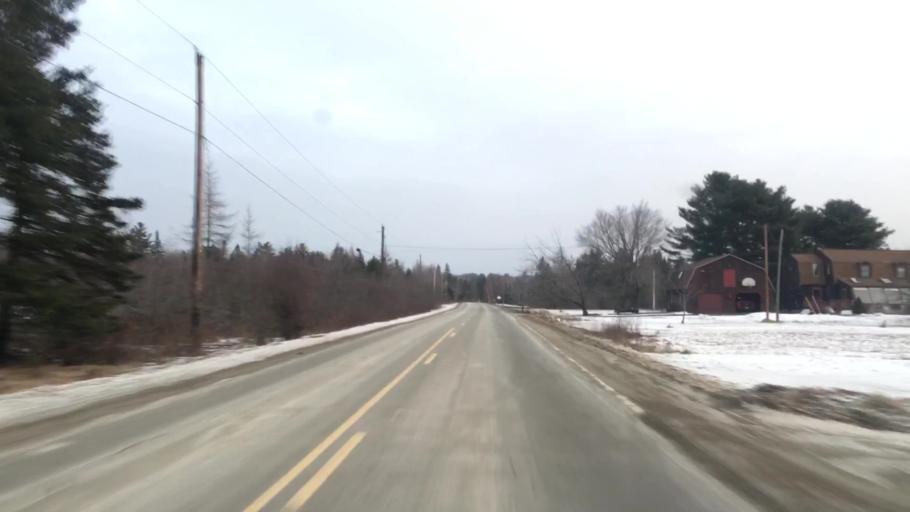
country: US
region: Maine
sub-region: Hancock County
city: Franklin
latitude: 44.6918
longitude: -68.3476
